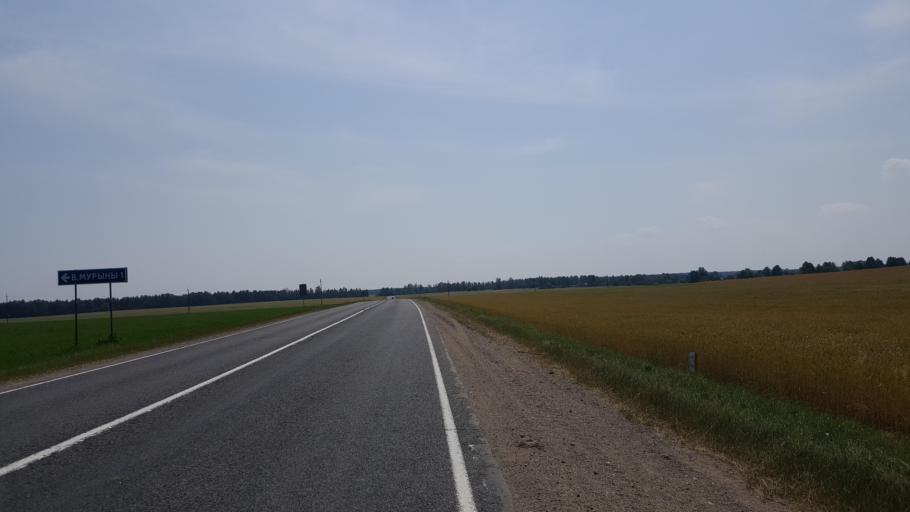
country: BY
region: Brest
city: Kamyanyets
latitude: 52.3811
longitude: 23.7888
